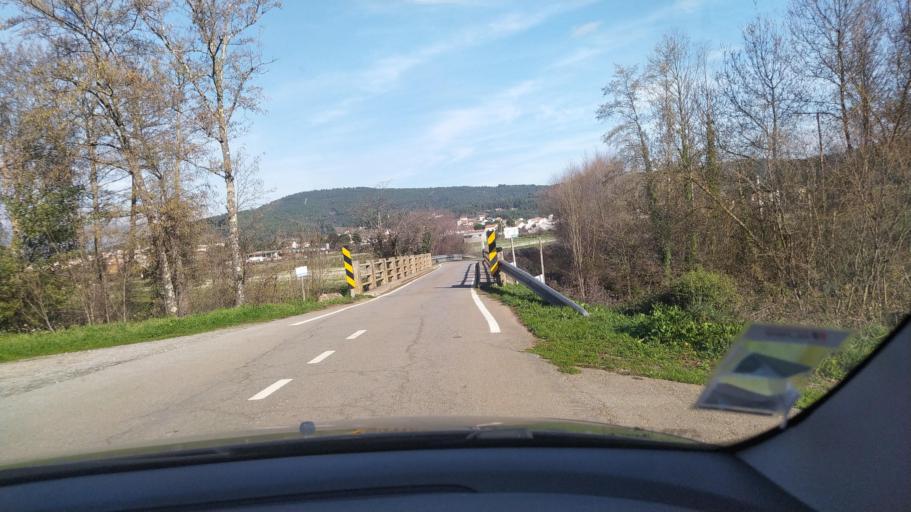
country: PT
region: Castelo Branco
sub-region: Concelho do Fundao
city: Aldeia de Joanes
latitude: 40.1879
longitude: -7.6429
